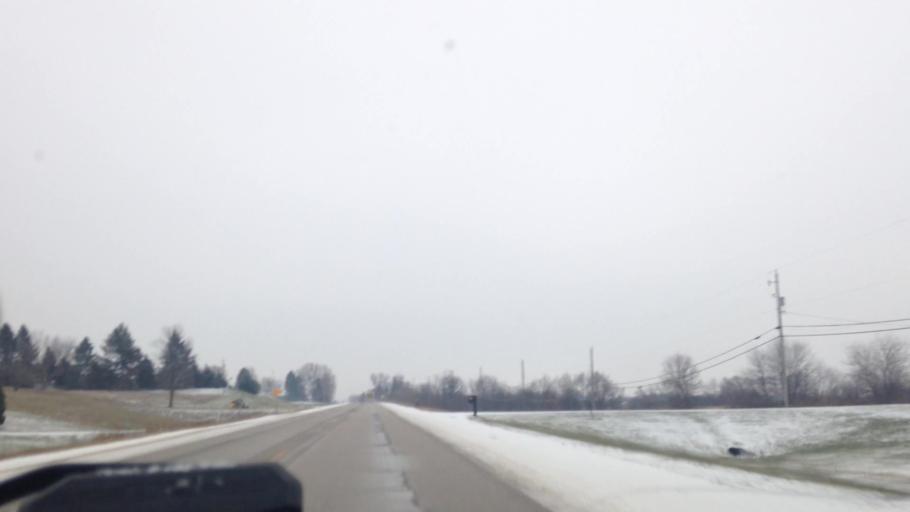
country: US
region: Wisconsin
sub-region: Dodge County
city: Mayville
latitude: 43.4319
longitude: -88.5421
